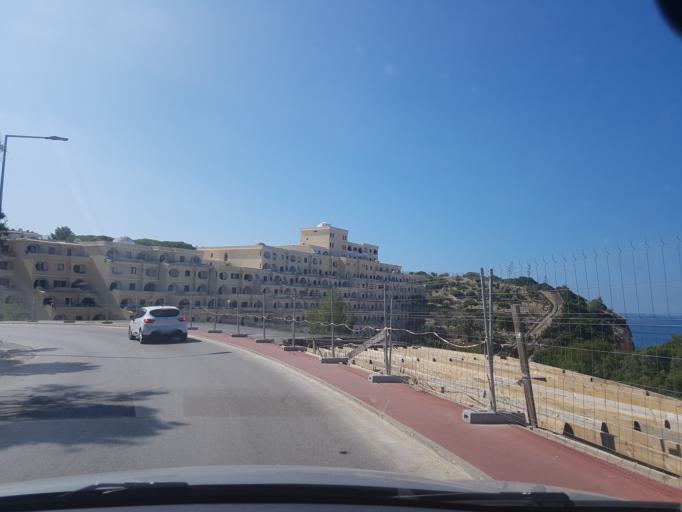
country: PT
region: Faro
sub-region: Lagoa
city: Carvoeiro
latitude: 37.0923
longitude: -8.4540
